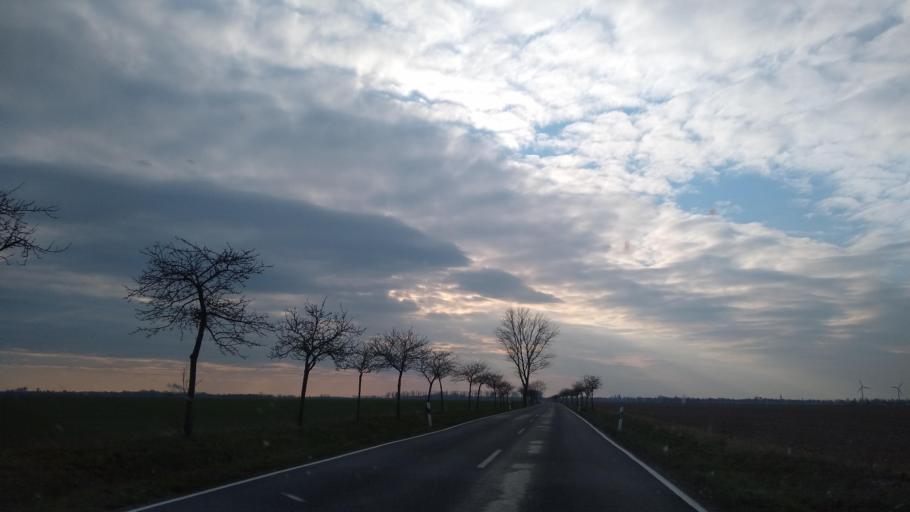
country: DE
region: Saxony
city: Wiedemar
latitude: 51.4719
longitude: 12.1858
